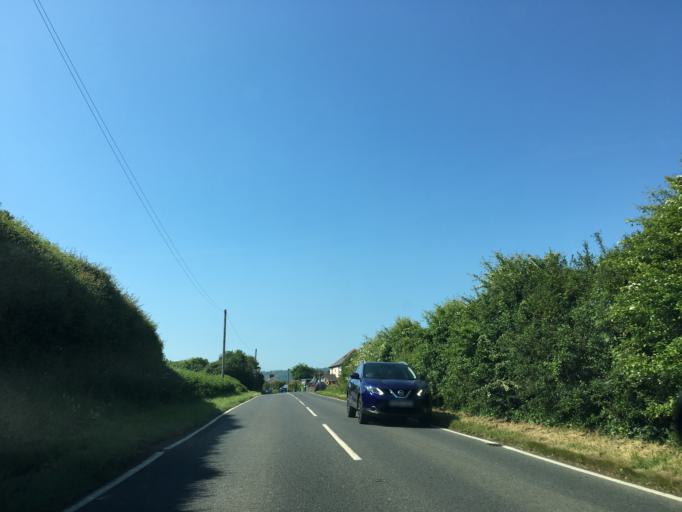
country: GB
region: England
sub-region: Isle of Wight
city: Newchurch
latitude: 50.6346
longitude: -1.2196
